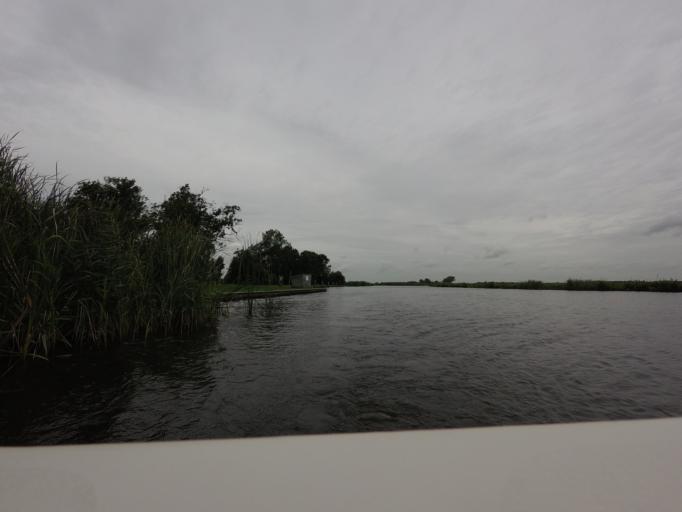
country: NL
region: Friesland
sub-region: Gemeente Boarnsterhim
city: Warten
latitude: 53.1153
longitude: 5.8866
